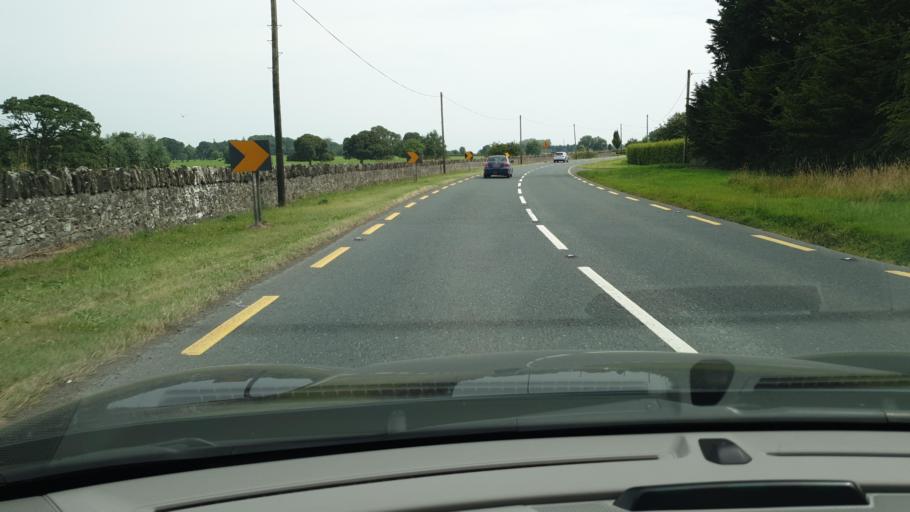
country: IE
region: Leinster
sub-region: An Mhi
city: Kells
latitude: 53.6996
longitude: -6.9297
